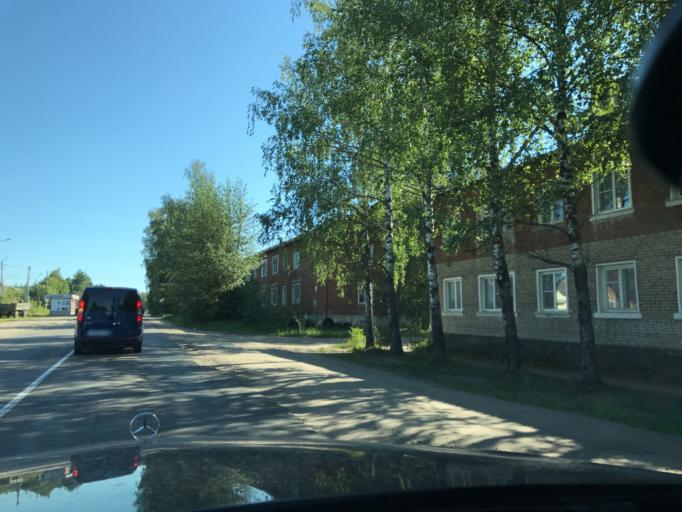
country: RU
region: Vladimir
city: Kirzhach
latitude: 56.1674
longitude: 38.8889
